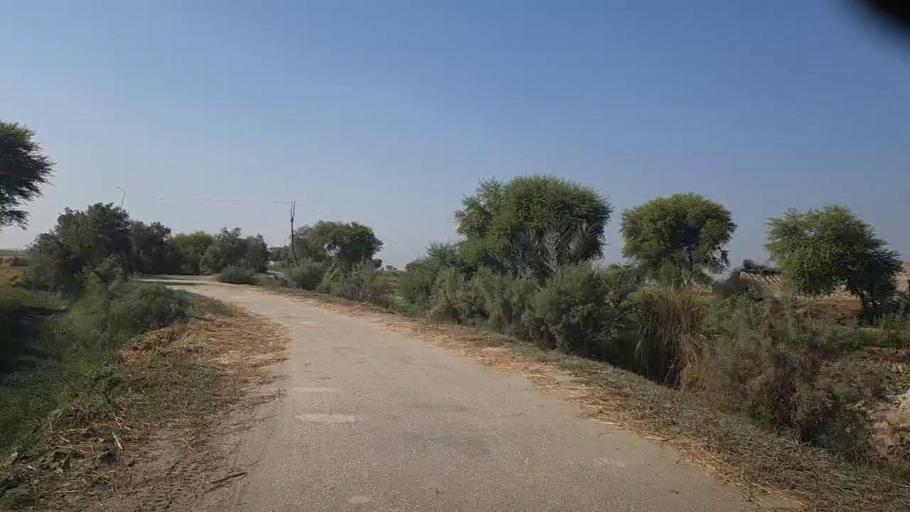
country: PK
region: Sindh
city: Tangwani
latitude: 28.2496
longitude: 68.9426
